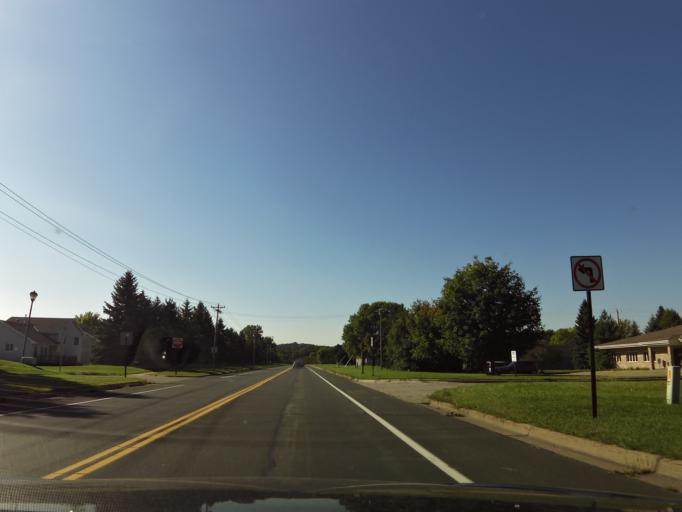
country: US
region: Minnesota
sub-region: Scott County
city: Savage
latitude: 44.7418
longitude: -93.3236
